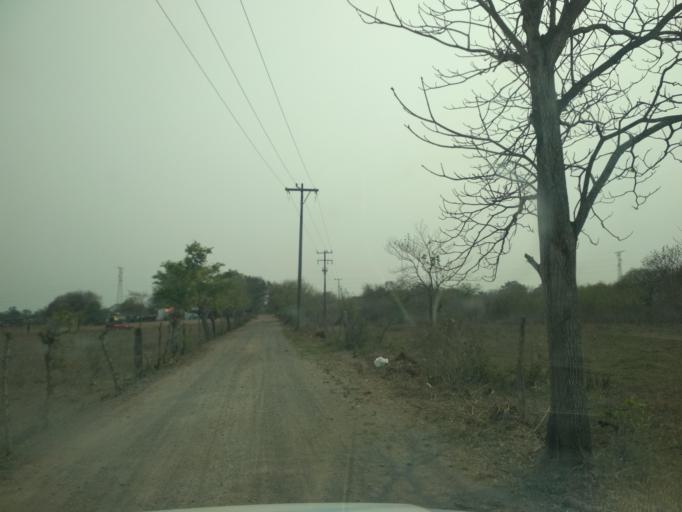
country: MX
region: Veracruz
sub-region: Veracruz
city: Delfino Victoria (Santa Fe)
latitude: 19.1884
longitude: -96.3010
